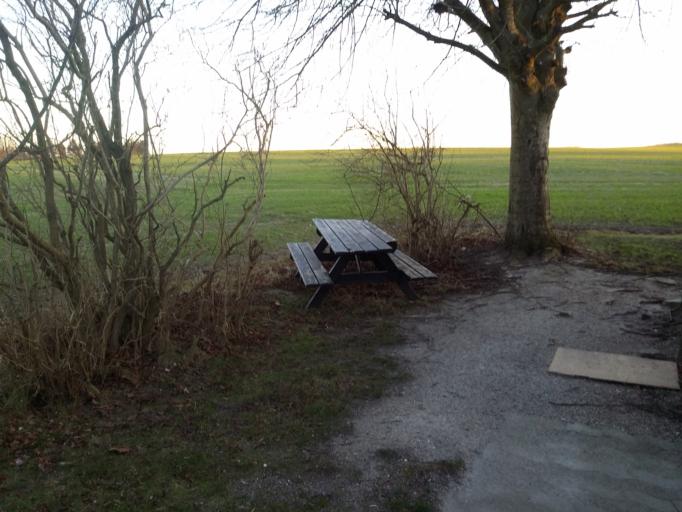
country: DK
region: Capital Region
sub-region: Frederikssund Kommune
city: Skibby
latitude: 55.7616
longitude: 11.9154
